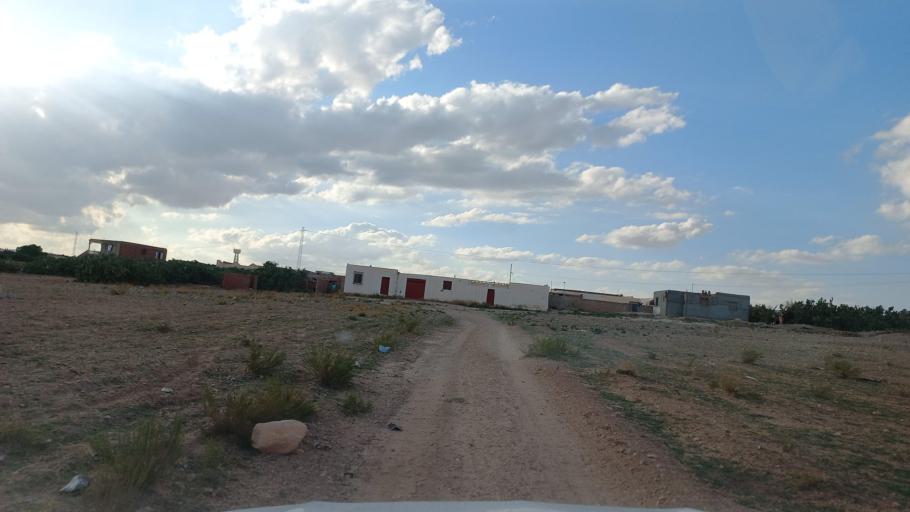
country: TN
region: Al Qasrayn
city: Sbiba
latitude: 35.3890
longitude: 9.0530
